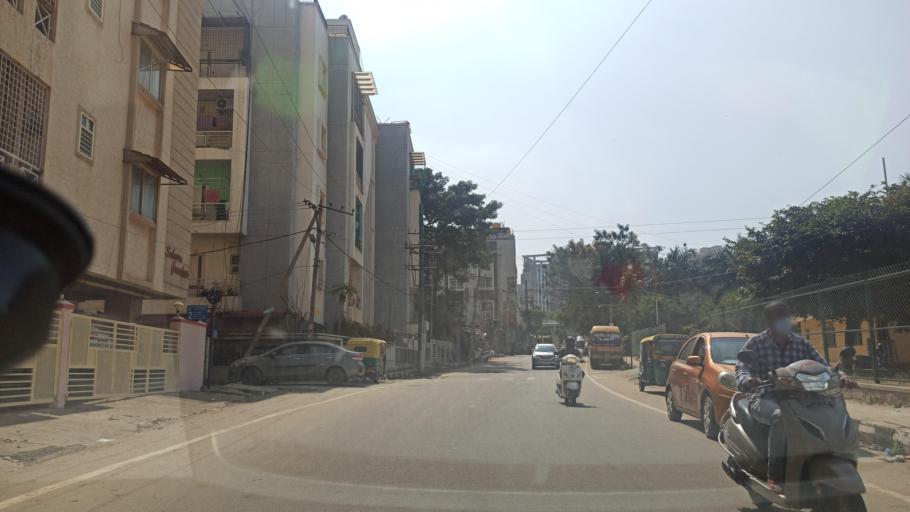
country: IN
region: Karnataka
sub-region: Bangalore Urban
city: Yelahanka
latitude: 13.0585
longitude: 77.5988
